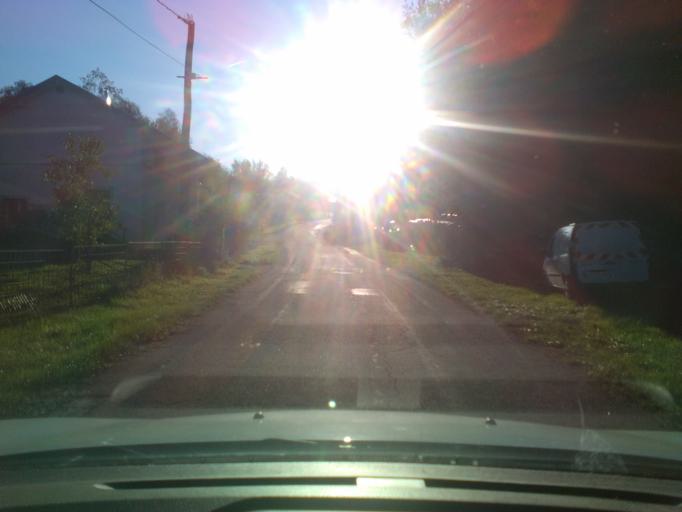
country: FR
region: Lorraine
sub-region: Departement des Vosges
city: Jeanmenil
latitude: 48.2946
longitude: 6.6829
